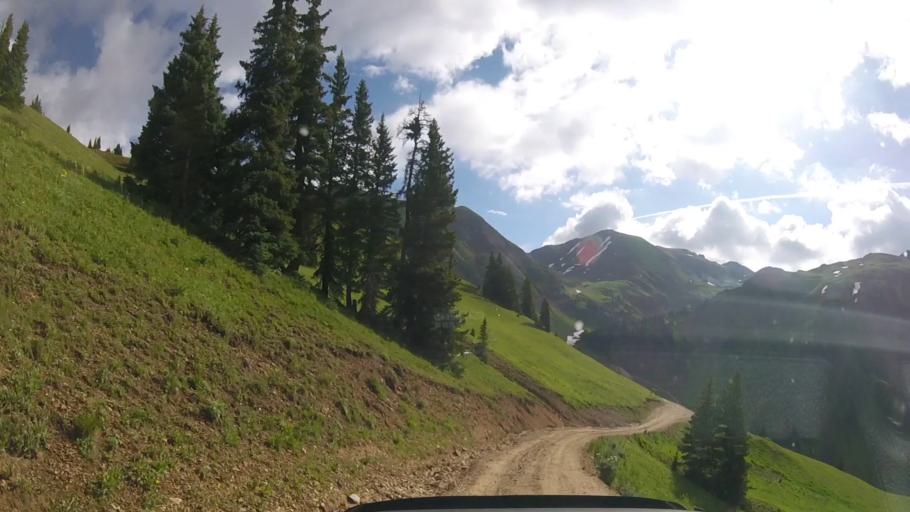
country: US
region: Colorado
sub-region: San Juan County
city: Silverton
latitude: 37.9072
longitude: -107.6493
